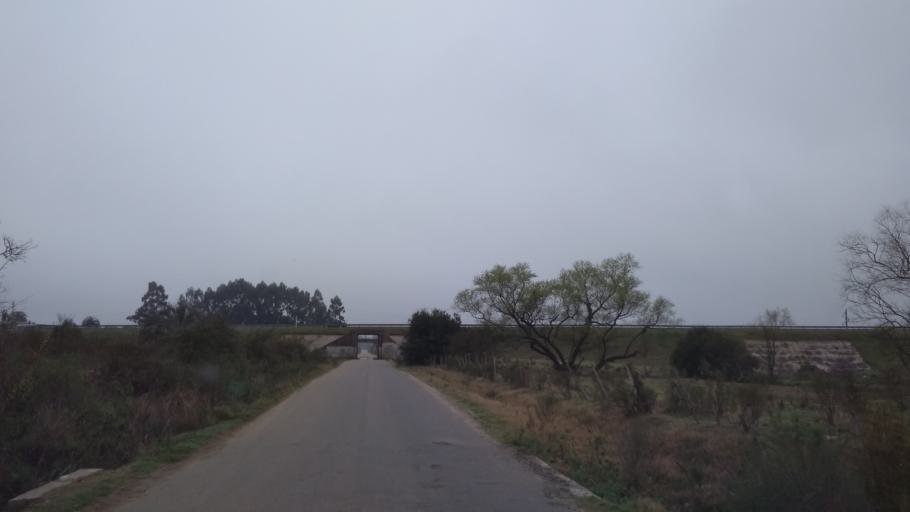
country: UY
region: Florida
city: Florida
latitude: -34.0892
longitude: -56.2085
